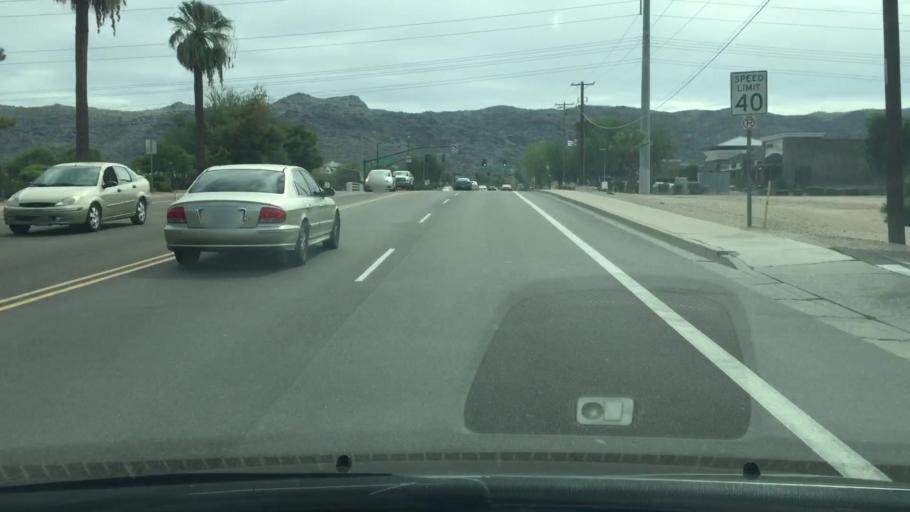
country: US
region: Arizona
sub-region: Maricopa County
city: Guadalupe
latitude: 33.3811
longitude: -112.0303
